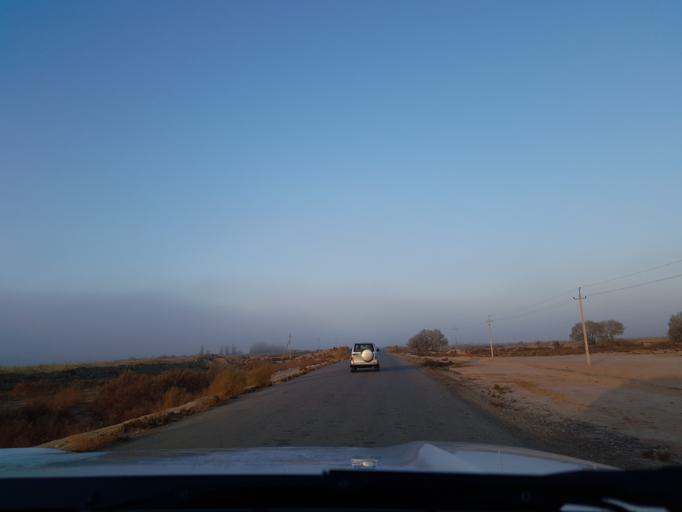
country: TM
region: Dasoguz
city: Koeneuergench
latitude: 41.8441
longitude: 58.6632
